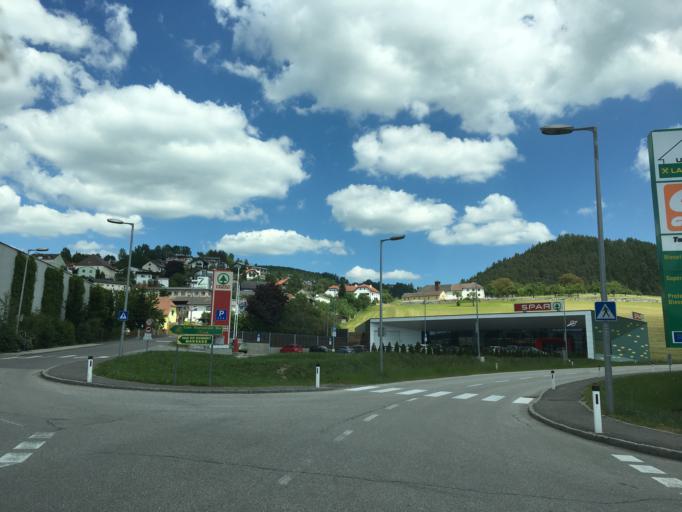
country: AT
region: Upper Austria
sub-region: Politischer Bezirk Freistadt
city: Freistadt
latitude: 48.4400
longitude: 14.5371
